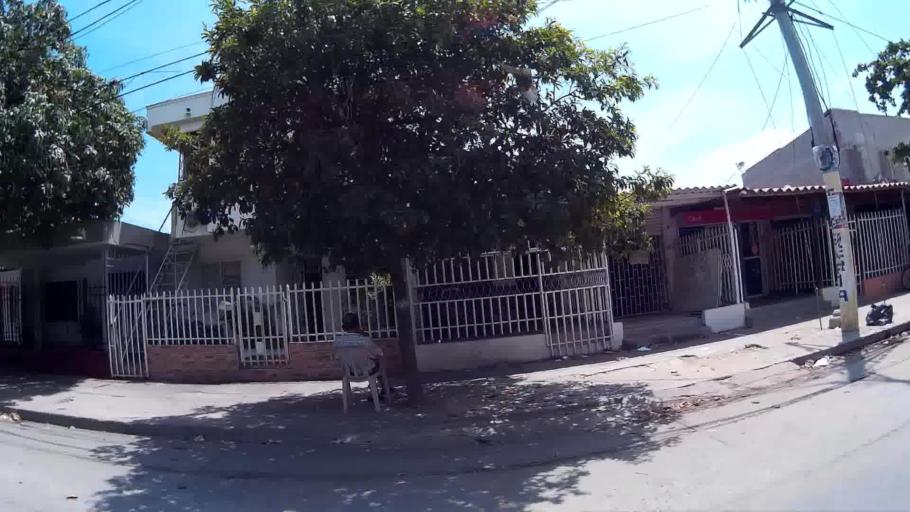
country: CO
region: Magdalena
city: Santa Marta
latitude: 11.2254
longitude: -74.1984
